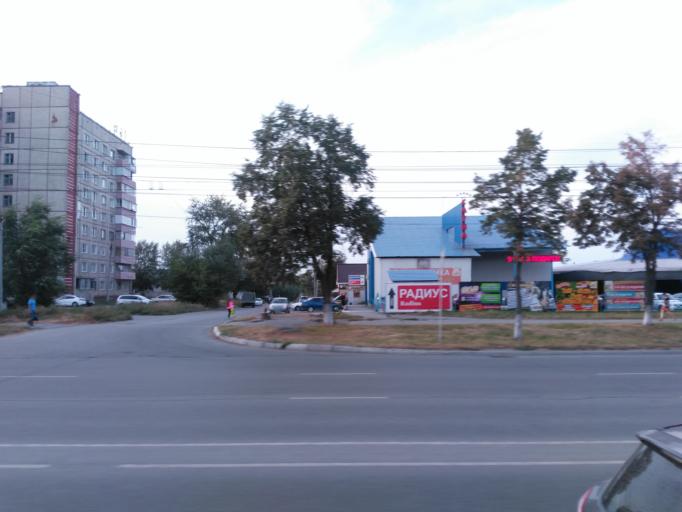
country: RU
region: Chelyabinsk
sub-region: Gorod Chelyabinsk
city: Chelyabinsk
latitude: 55.1919
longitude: 61.3675
